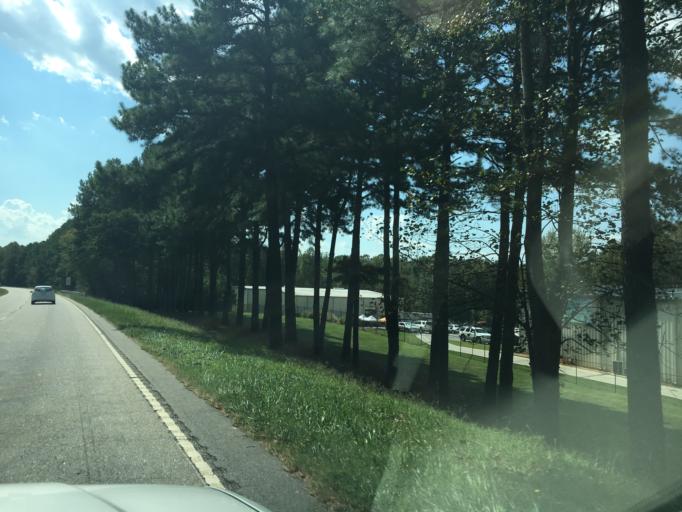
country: US
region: South Carolina
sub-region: Pickens County
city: Liberty
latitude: 34.7495
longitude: -82.7103
